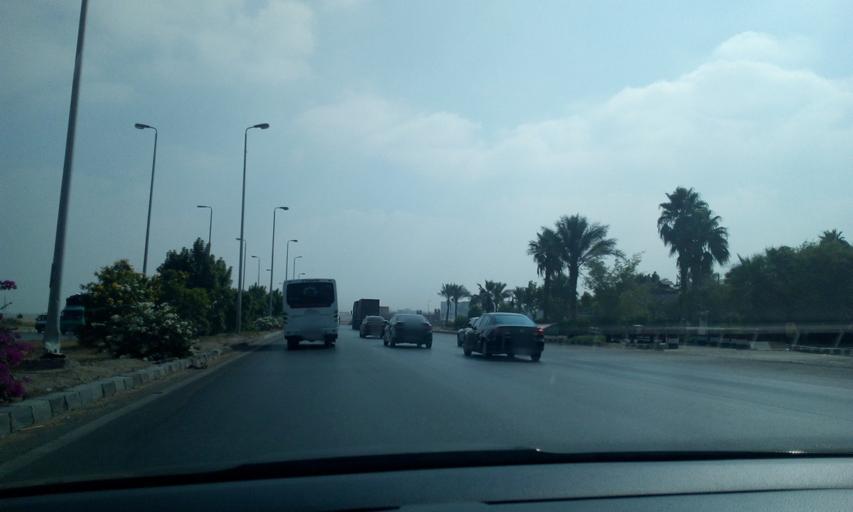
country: EG
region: Eastern Province
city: Bilbays
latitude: 30.2474
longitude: 31.7297
